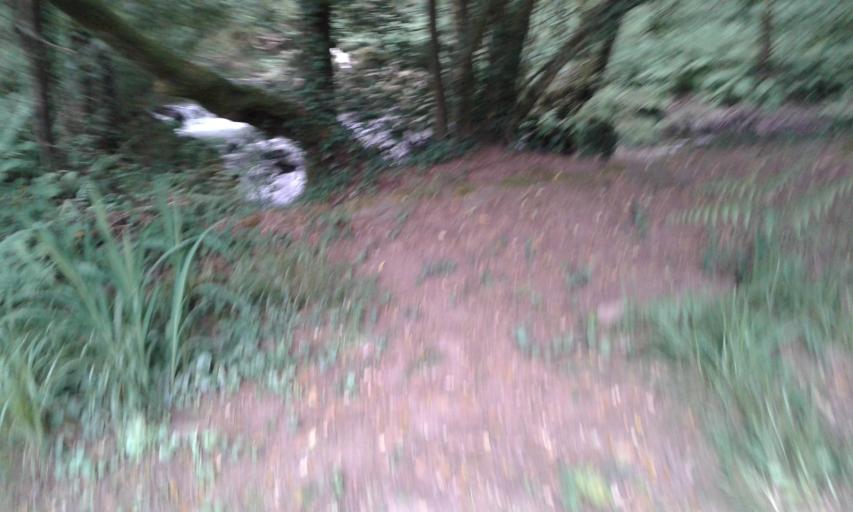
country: ES
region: Galicia
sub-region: Provincia de Pontevedra
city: Gondomar
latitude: 42.1168
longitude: -8.7598
